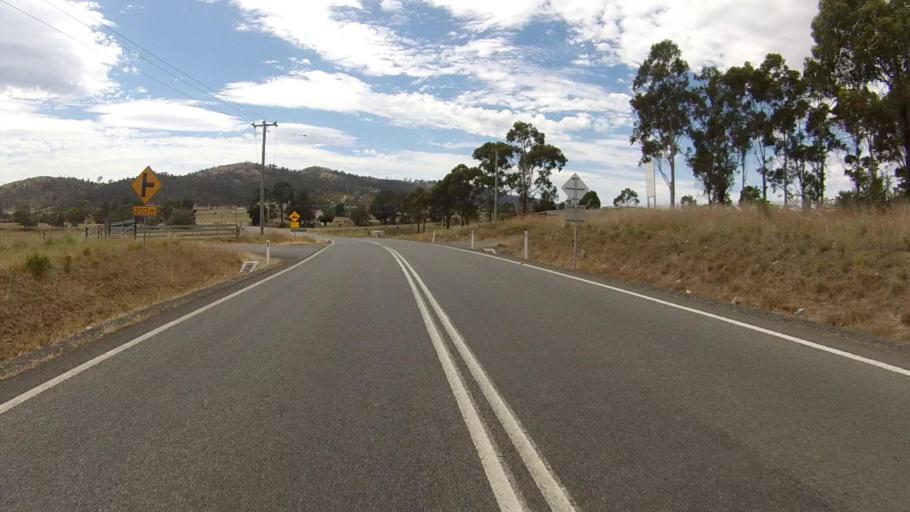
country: AU
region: Tasmania
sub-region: Brighton
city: Old Beach
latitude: -42.6926
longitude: 147.3412
